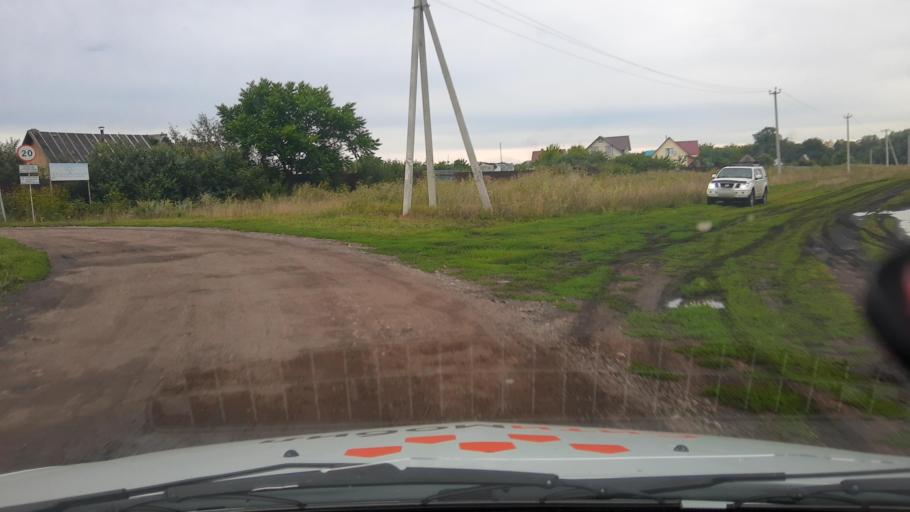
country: RU
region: Bashkortostan
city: Ufa
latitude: 54.5710
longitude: 55.9493
